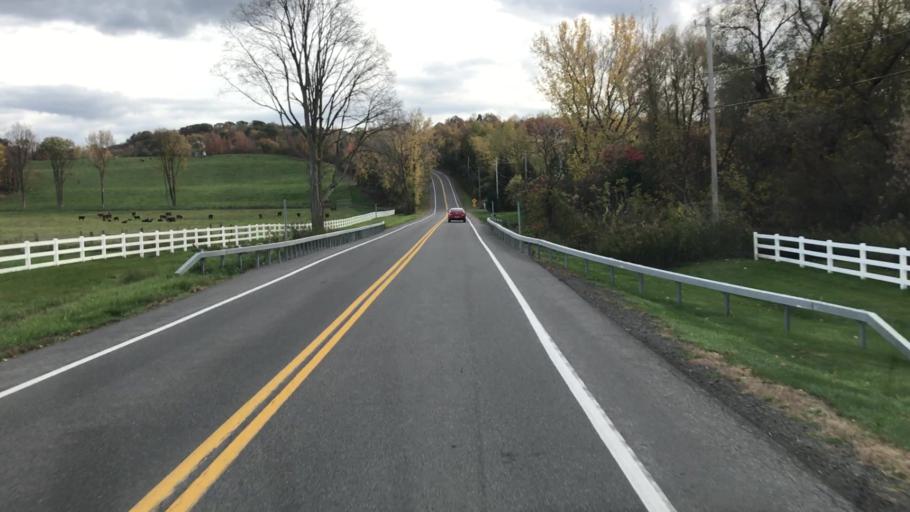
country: US
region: New York
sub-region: Onondaga County
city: Fayetteville
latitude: 42.9904
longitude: -76.0451
